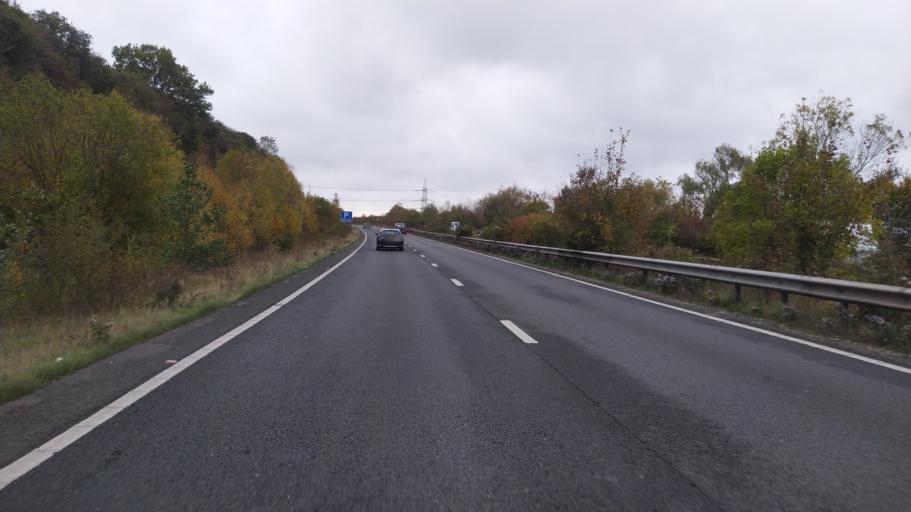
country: GB
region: England
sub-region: Hampshire
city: Cowplain
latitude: 50.9369
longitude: -0.9918
